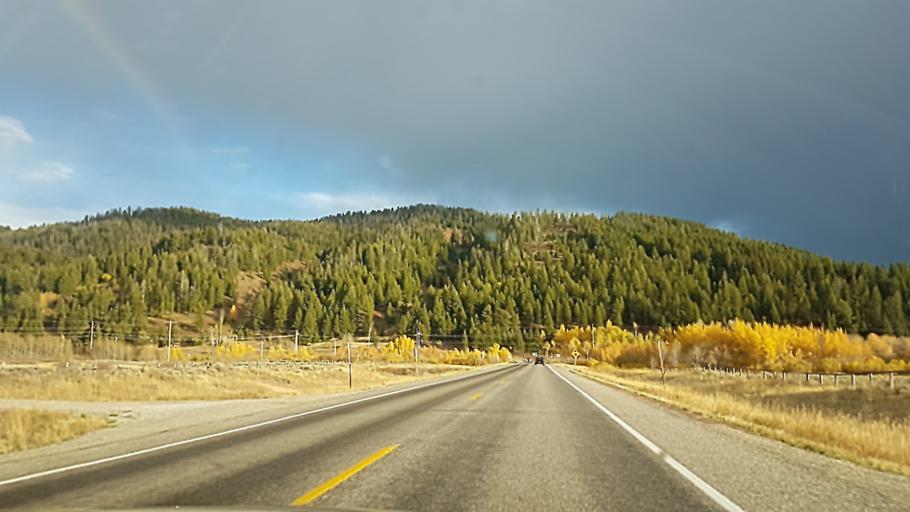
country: US
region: Montana
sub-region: Gallatin County
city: West Yellowstone
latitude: 44.6367
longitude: -111.3305
